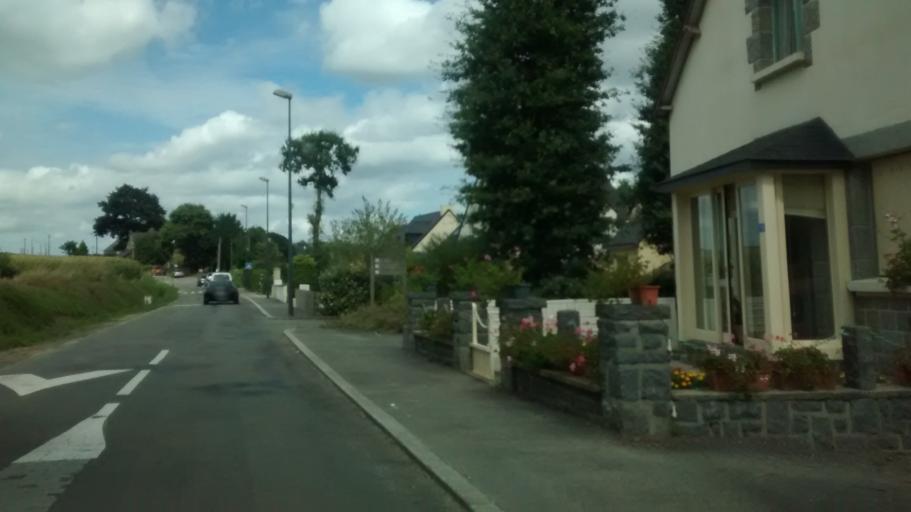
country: FR
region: Brittany
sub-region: Departement d'Ille-et-Vilaine
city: Tinteniac
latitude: 48.2937
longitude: -1.8488
